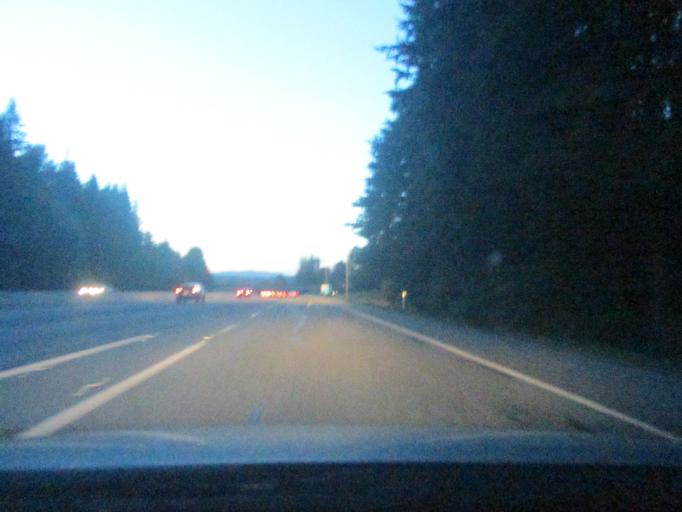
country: US
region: Washington
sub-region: Snohomish County
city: Smokey Point
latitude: 48.1734
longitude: -122.1923
